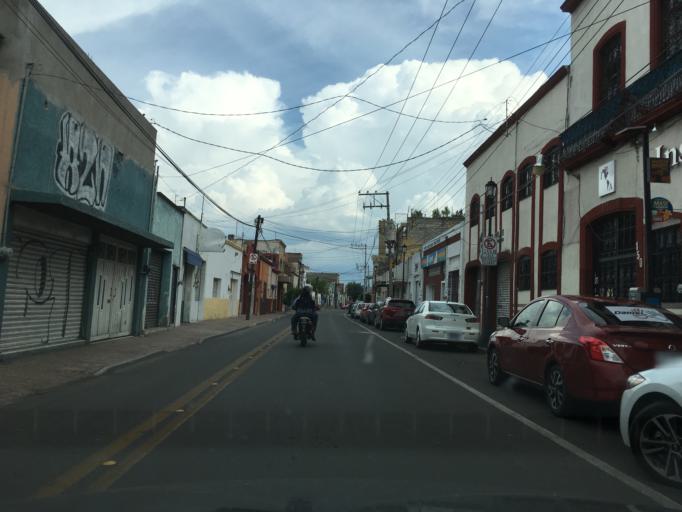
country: MX
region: Guanajuato
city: Celaya
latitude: 20.5259
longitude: -100.8178
